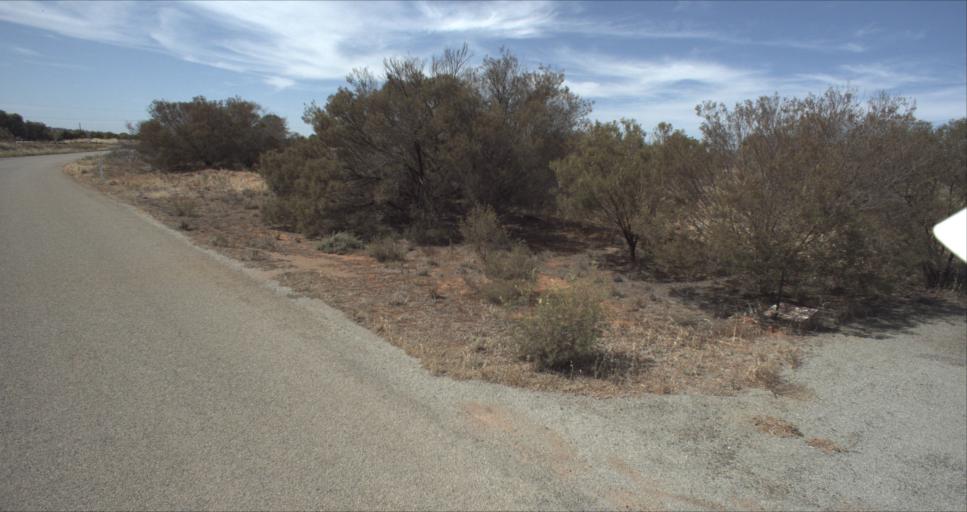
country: AU
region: New South Wales
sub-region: Leeton
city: Leeton
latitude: -34.5721
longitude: 146.4527
